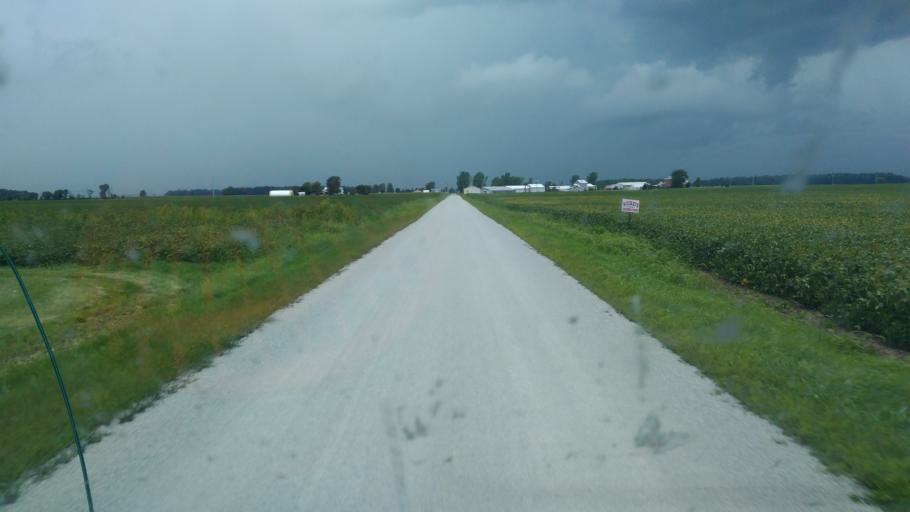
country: US
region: Ohio
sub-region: Hardin County
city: Kenton
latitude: 40.6757
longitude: -83.5145
